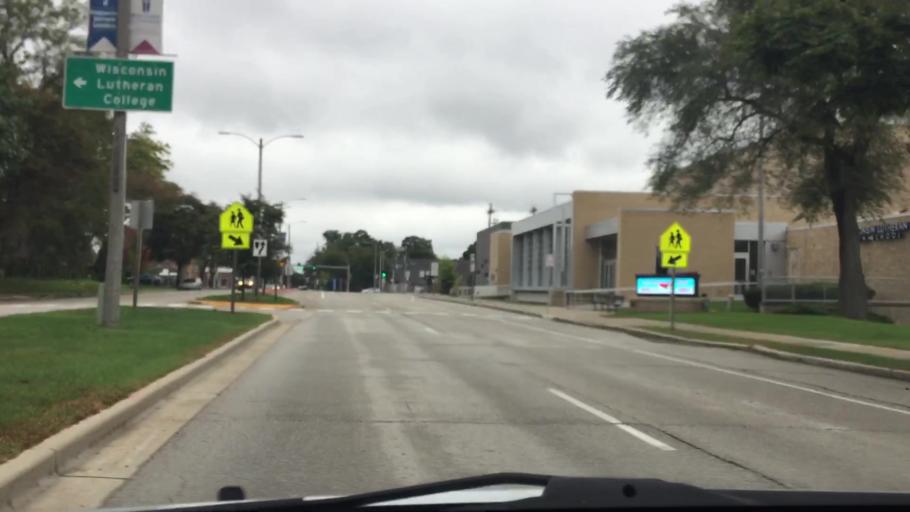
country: US
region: Wisconsin
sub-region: Milwaukee County
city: Wauwatosa
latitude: 43.0342
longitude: -88.0166
